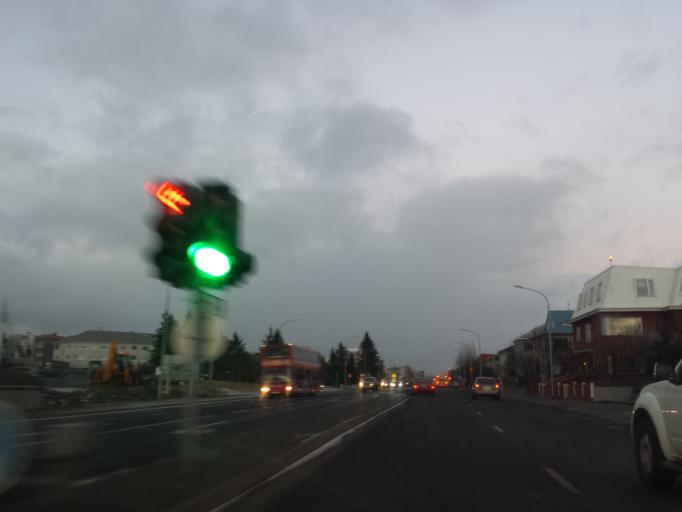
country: IS
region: Capital Region
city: Kopavogur
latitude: 64.1369
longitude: -21.9231
